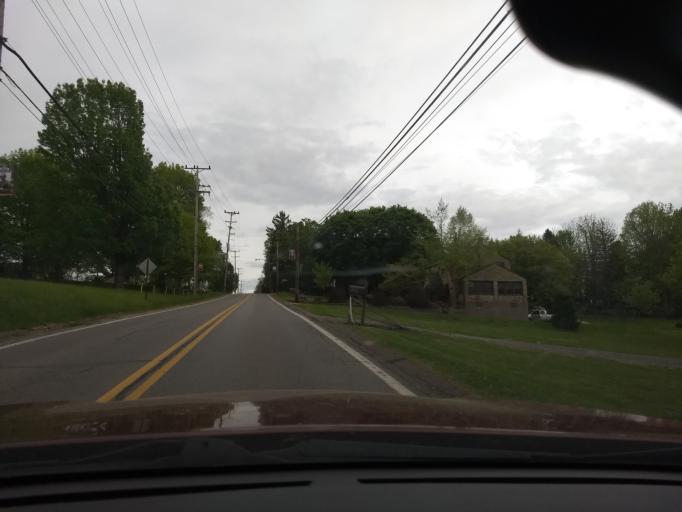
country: US
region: Pennsylvania
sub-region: Allegheny County
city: Coraopolis
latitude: 40.4839
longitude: -80.1371
